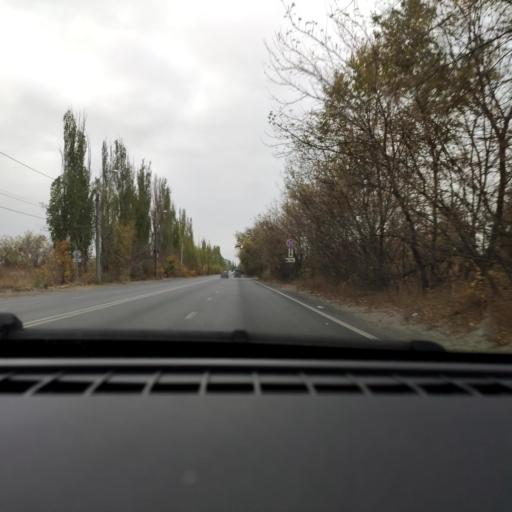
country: RU
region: Voronezj
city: Maslovka
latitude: 51.6115
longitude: 39.2570
